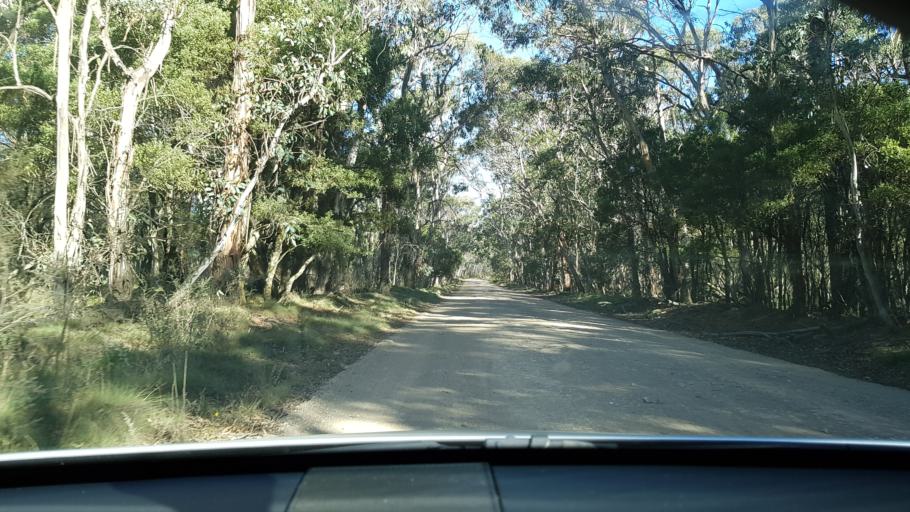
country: AU
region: New South Wales
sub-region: Oberon
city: Oberon
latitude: -33.9351
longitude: 150.0644
